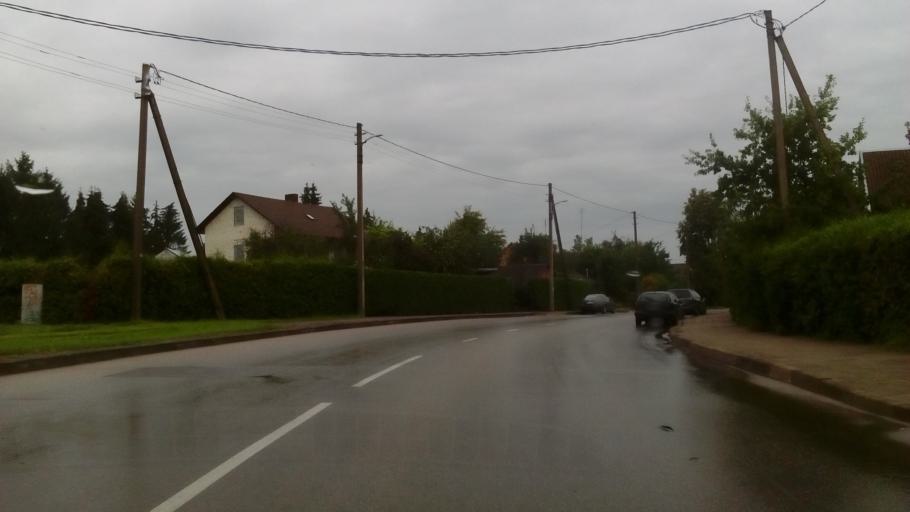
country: LT
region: Alytaus apskritis
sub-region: Alytus
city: Alytus
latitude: 54.3899
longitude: 24.0401
